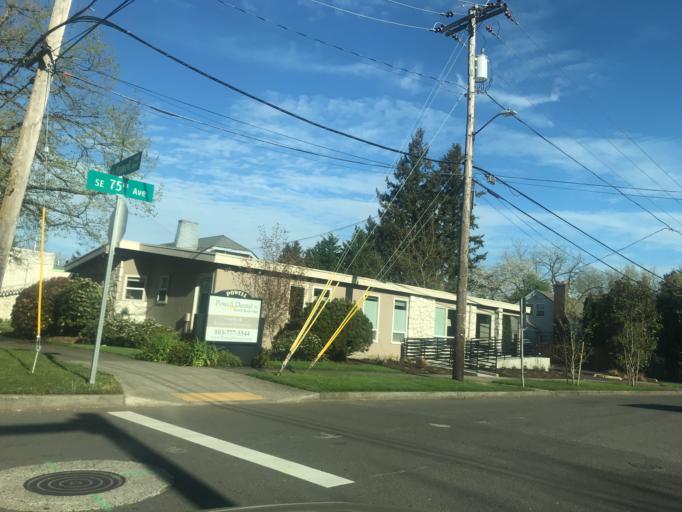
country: US
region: Oregon
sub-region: Multnomah County
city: Lents
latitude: 45.4974
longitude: -122.5857
